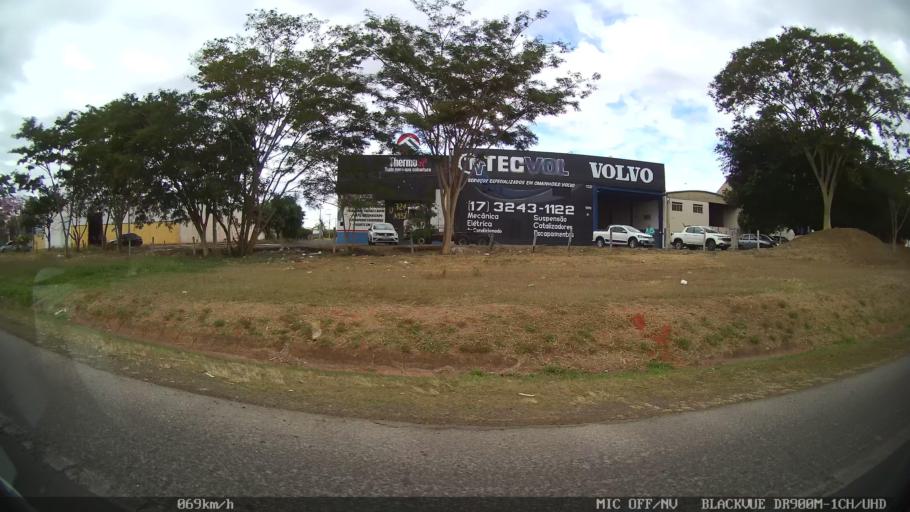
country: BR
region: Sao Paulo
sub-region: Bady Bassitt
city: Bady Bassitt
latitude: -20.8062
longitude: -49.5228
